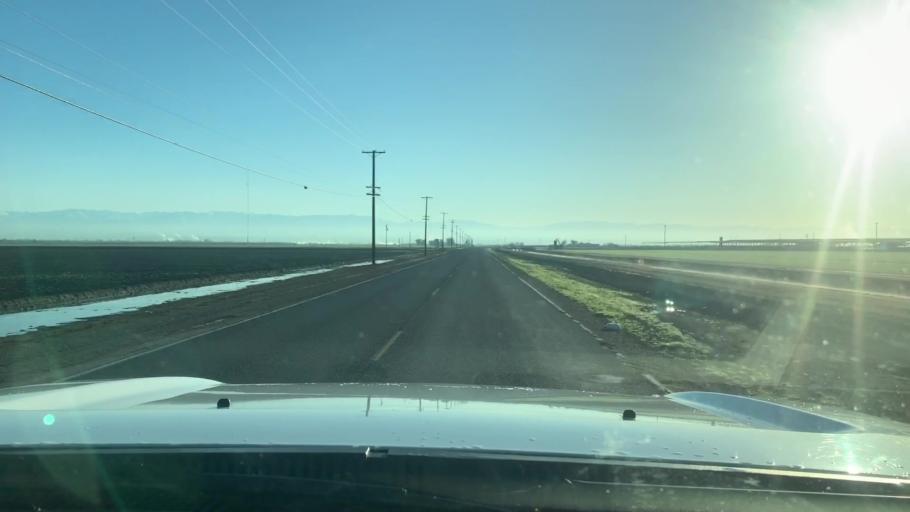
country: US
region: California
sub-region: Tulare County
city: Tulare
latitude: 36.1817
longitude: -119.4149
